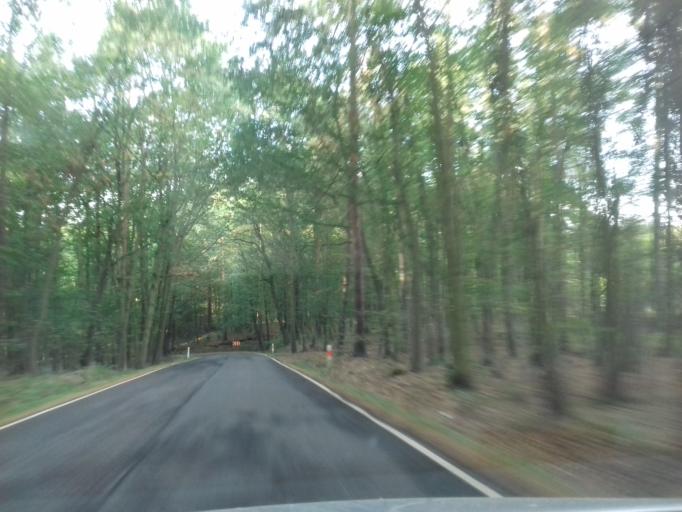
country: CZ
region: Central Bohemia
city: Kamenny Privoz
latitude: 49.8517
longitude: 14.5063
